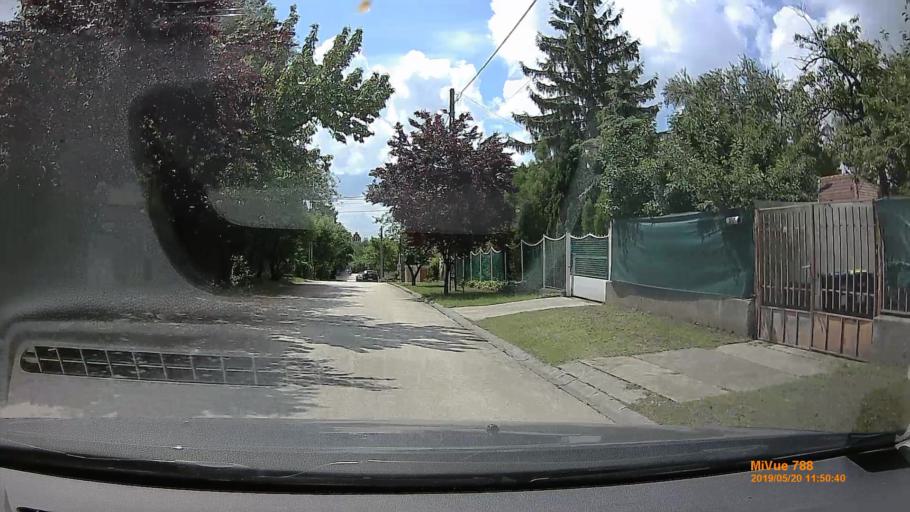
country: HU
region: Budapest
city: Budapest XVII. keruelet
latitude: 47.4954
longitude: 19.2581
